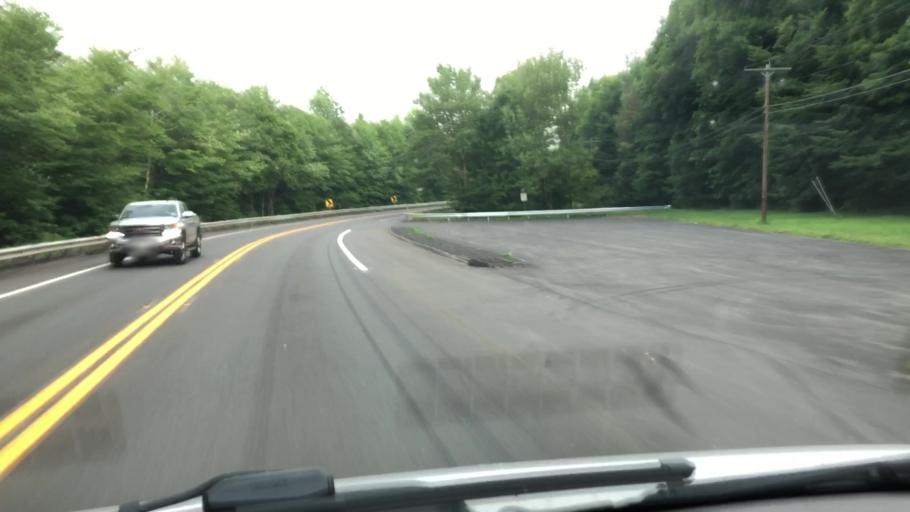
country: US
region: Massachusetts
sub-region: Hampshire County
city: Chesterfield
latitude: 42.4496
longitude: -72.8198
